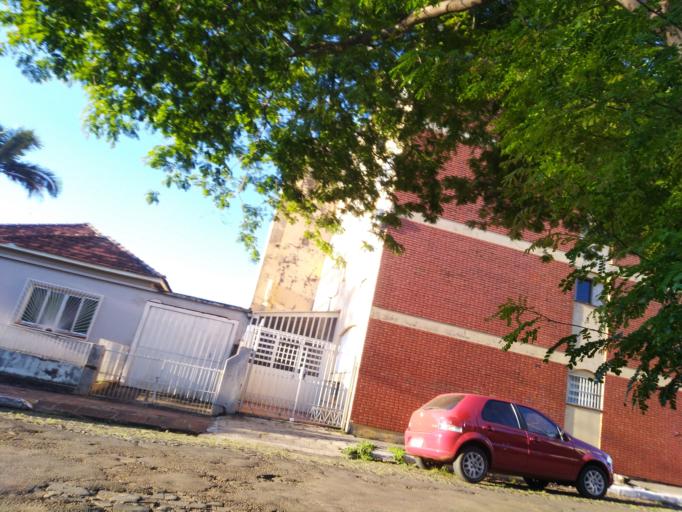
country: BR
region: Rio Grande do Sul
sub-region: Sao Borja
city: Sao Borja
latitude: -28.6613
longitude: -56.0078
